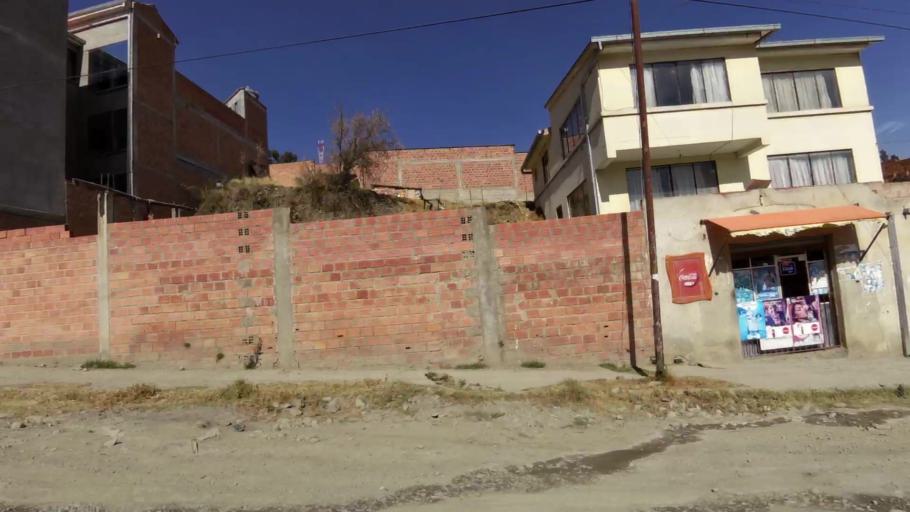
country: BO
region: La Paz
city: La Paz
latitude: -16.5069
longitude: -68.0511
